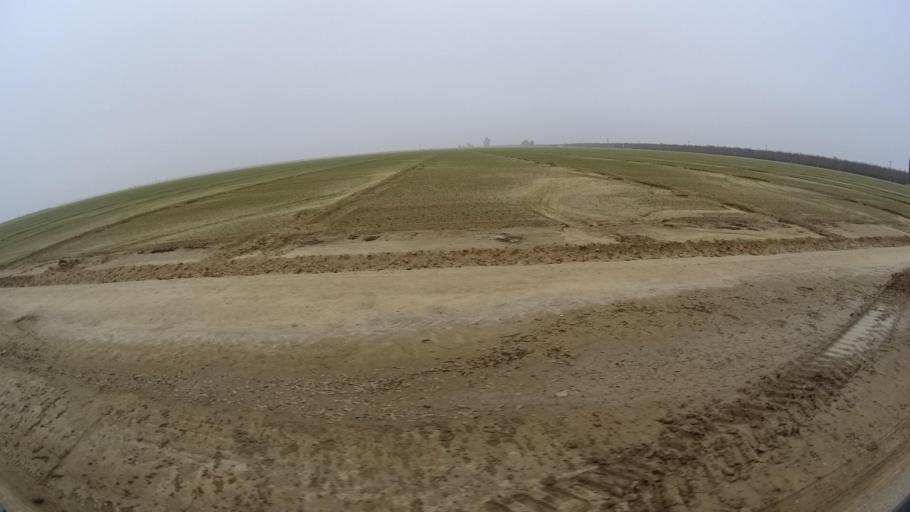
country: US
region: California
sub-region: Kern County
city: Lost Hills
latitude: 35.5866
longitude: -119.5289
